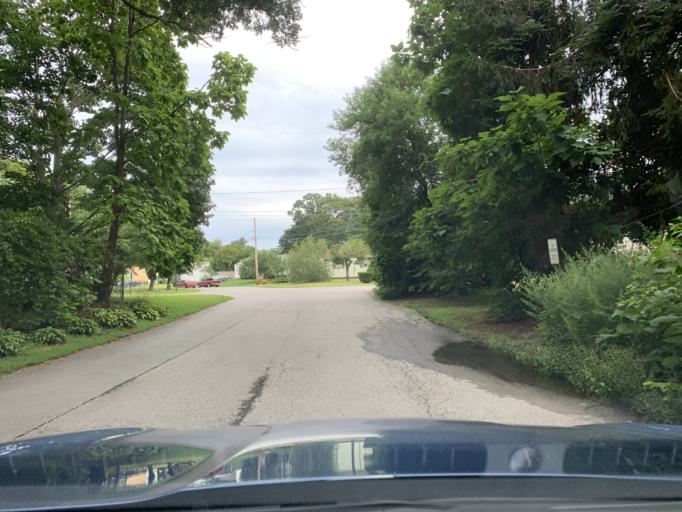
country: US
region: Rhode Island
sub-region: Kent County
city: East Greenwich
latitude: 41.6105
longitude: -71.4665
